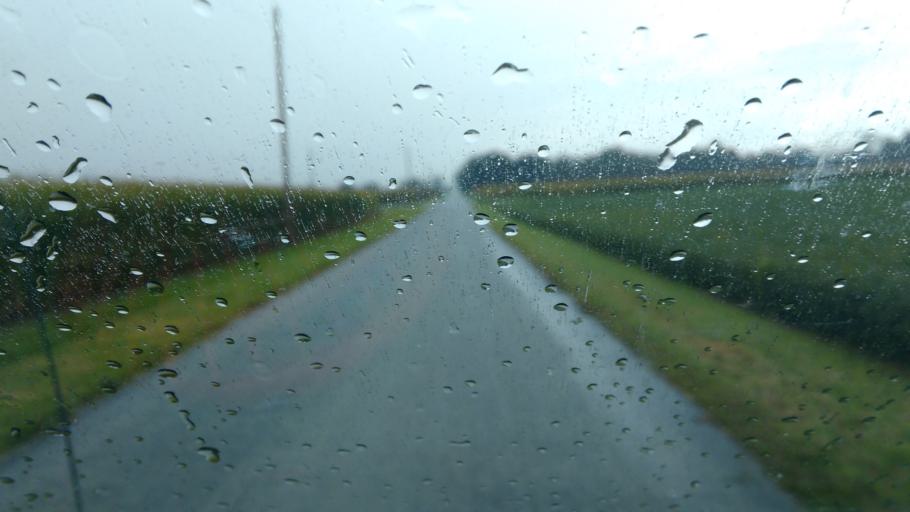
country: US
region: Ohio
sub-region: Hardin County
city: Kenton
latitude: 40.7170
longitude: -83.5712
